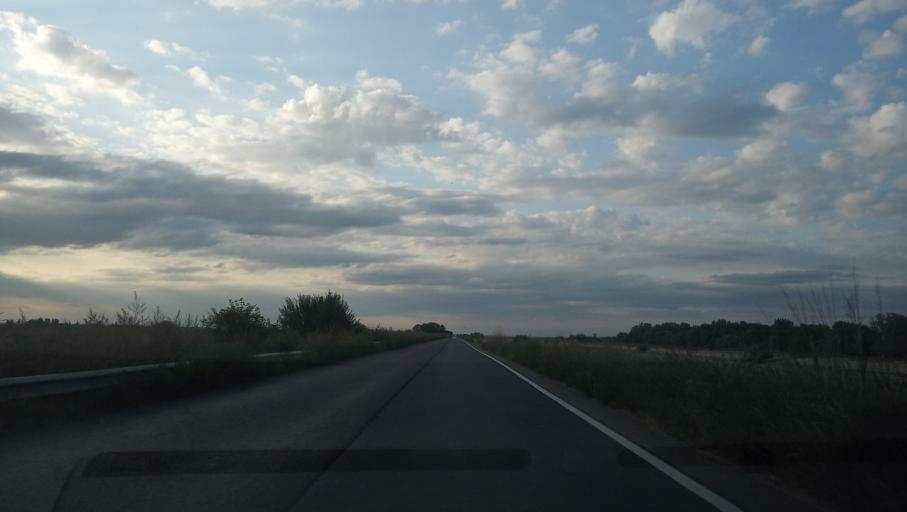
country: RO
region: Calarasi
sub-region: Municipiul Calarasi
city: Calarasi
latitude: 44.1796
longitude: 27.3054
